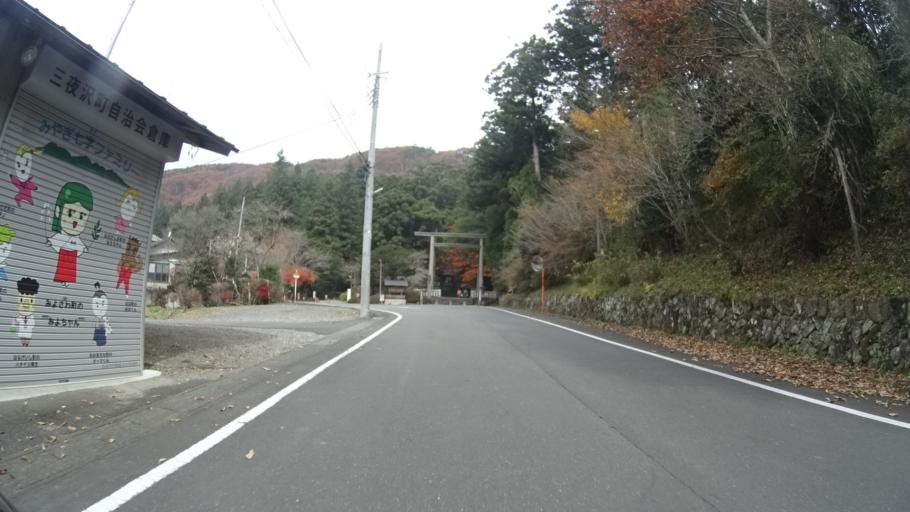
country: JP
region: Gunma
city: Omamacho-omama
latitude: 36.4831
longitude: 139.1776
